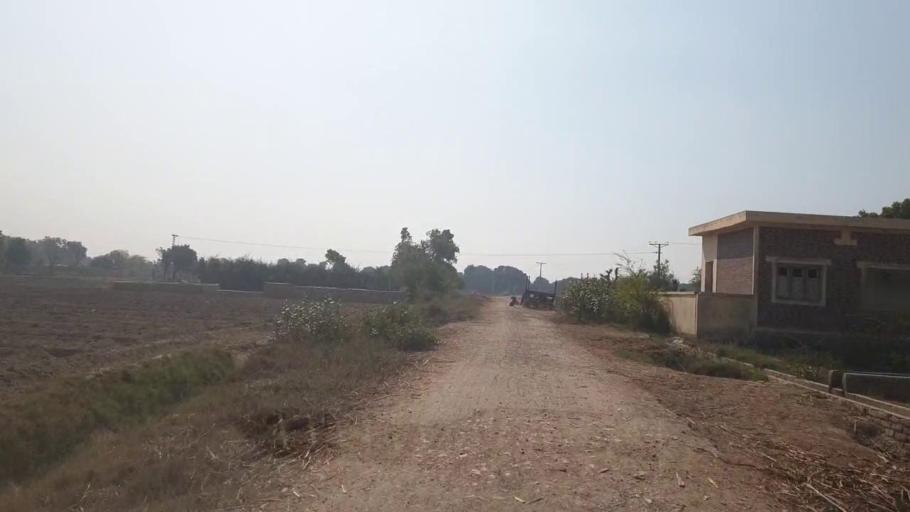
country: PK
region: Sindh
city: Tando Adam
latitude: 25.6250
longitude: 68.7353
